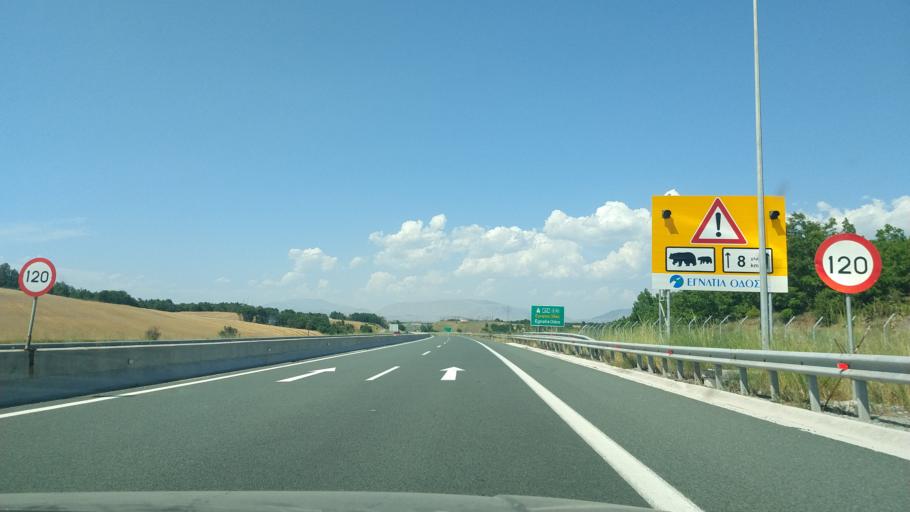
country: GR
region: West Macedonia
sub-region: Nomos Grevenon
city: Grevena
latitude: 40.0710
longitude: 21.4429
